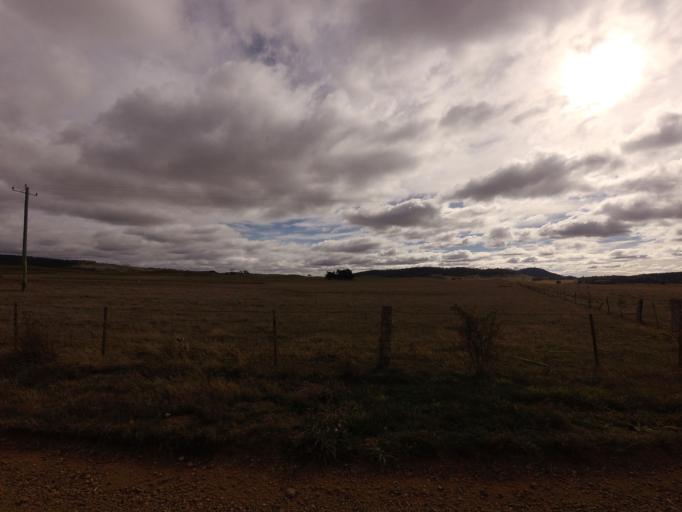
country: AU
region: Tasmania
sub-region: Brighton
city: Bridgewater
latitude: -42.4238
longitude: 147.3906
